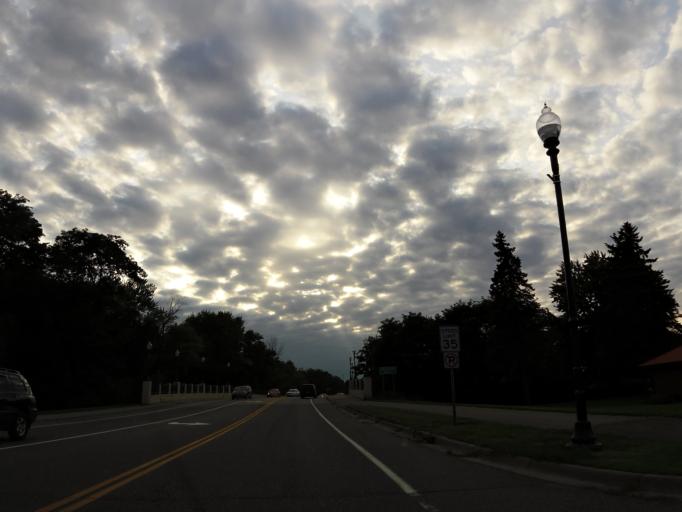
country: US
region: Minnesota
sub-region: Dakota County
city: Farmington
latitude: 44.6405
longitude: -93.1506
